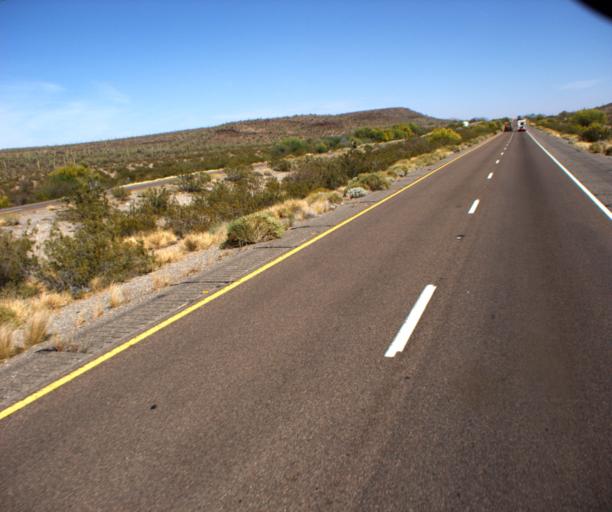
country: US
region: Arizona
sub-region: Pinal County
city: Maricopa
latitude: 32.8494
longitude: -112.3331
